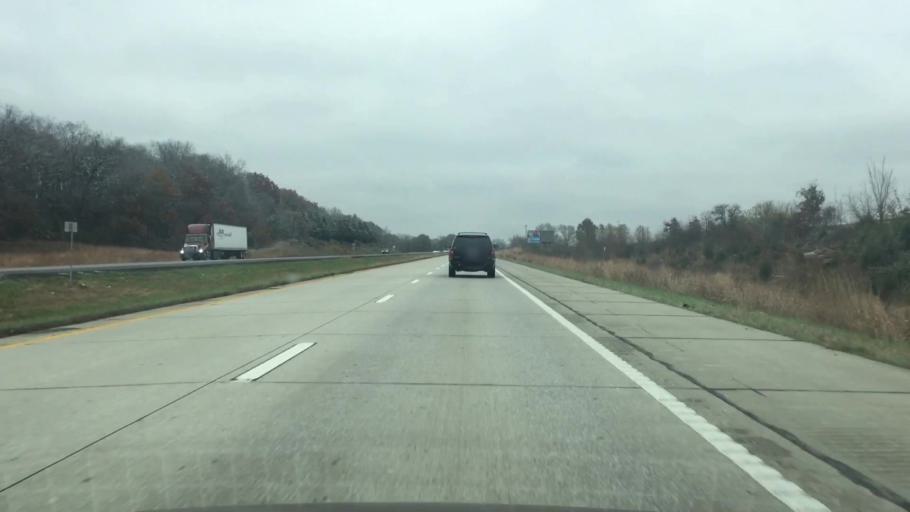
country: US
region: Missouri
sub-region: Saint Clair County
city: Osceola
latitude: 38.0167
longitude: -93.6640
